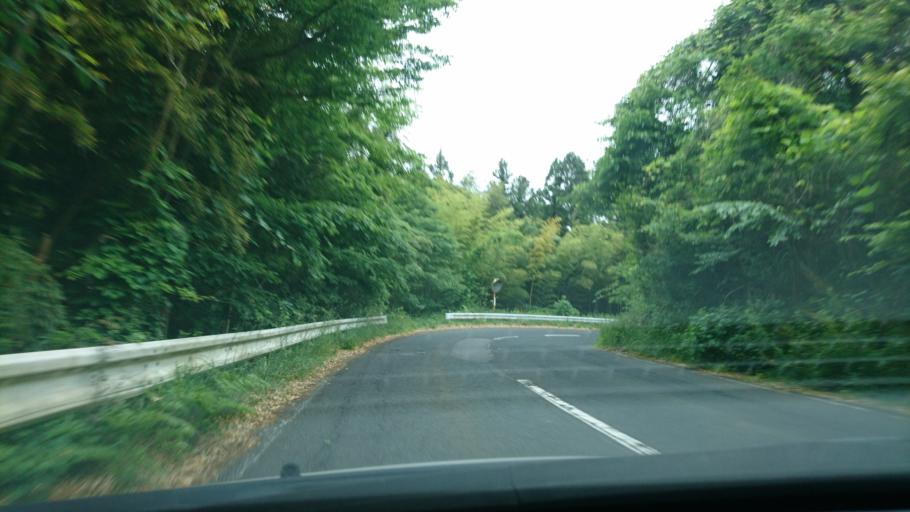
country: JP
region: Iwate
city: Ichinoseki
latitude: 38.9434
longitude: 141.2744
